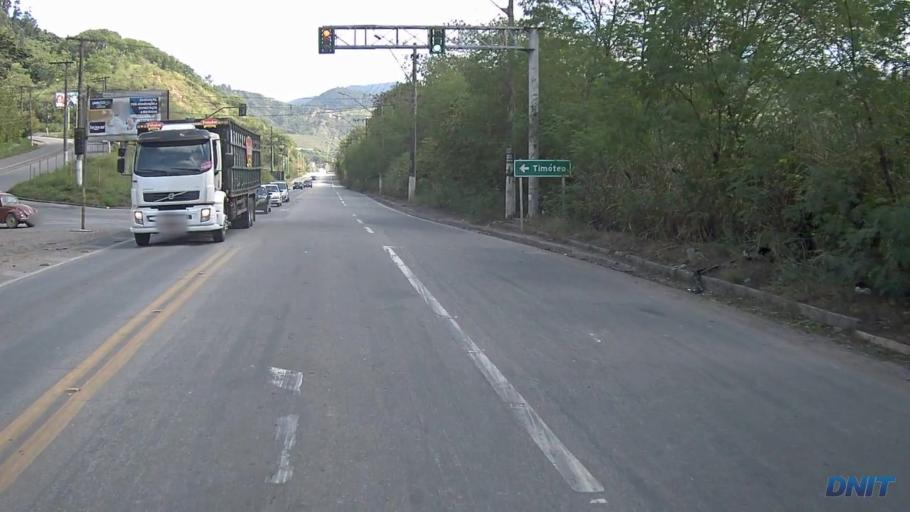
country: BR
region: Minas Gerais
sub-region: Coronel Fabriciano
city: Coronel Fabriciano
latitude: -19.5286
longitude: -42.6507
